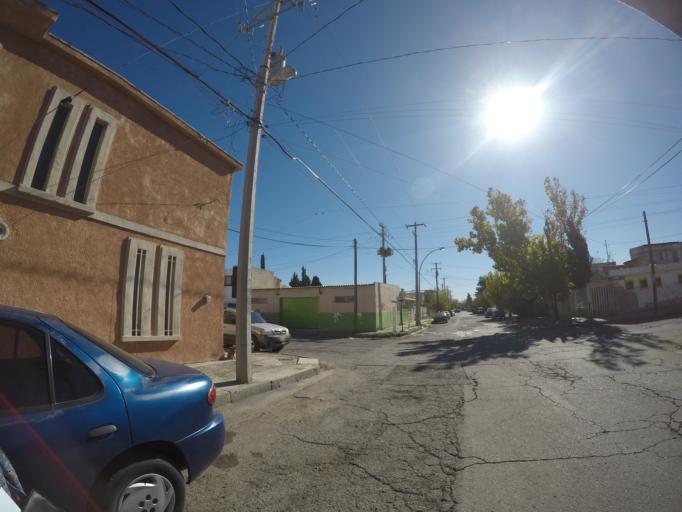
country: MX
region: Chihuahua
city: Ciudad Juarez
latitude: 31.7414
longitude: -106.4610
